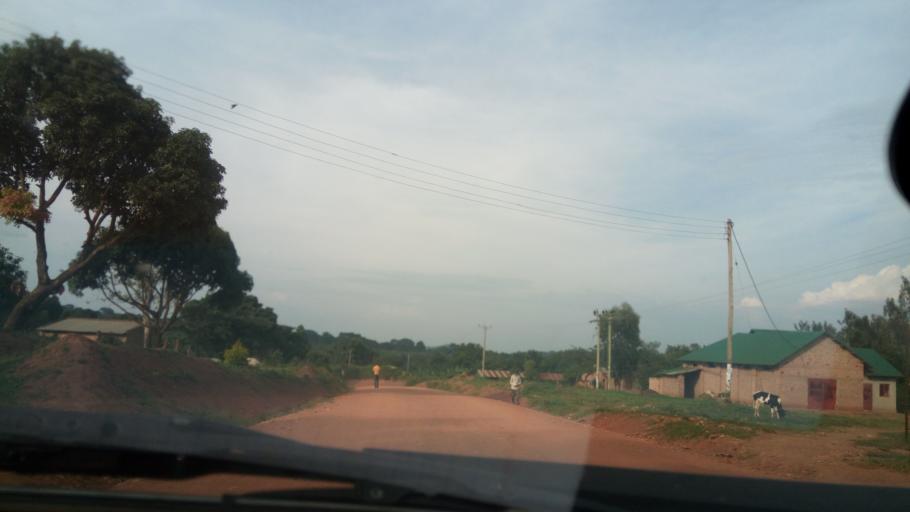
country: UG
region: Central Region
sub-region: Mityana District
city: Mityana
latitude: 0.5012
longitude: 32.1396
